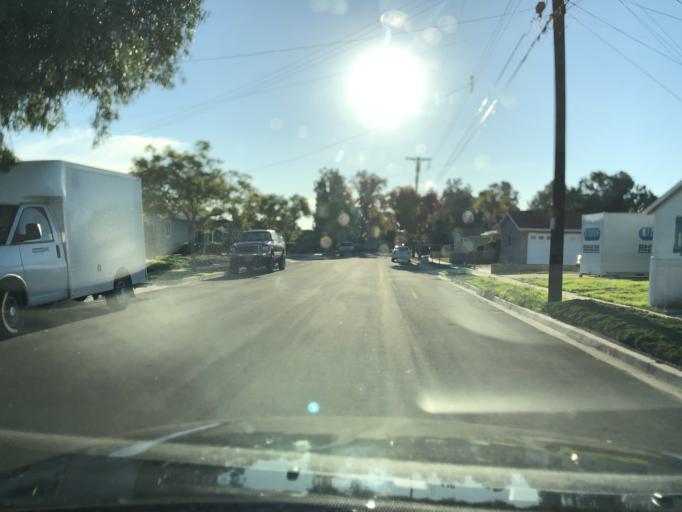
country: US
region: California
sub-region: San Diego County
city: La Jolla
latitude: 32.8197
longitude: -117.1902
